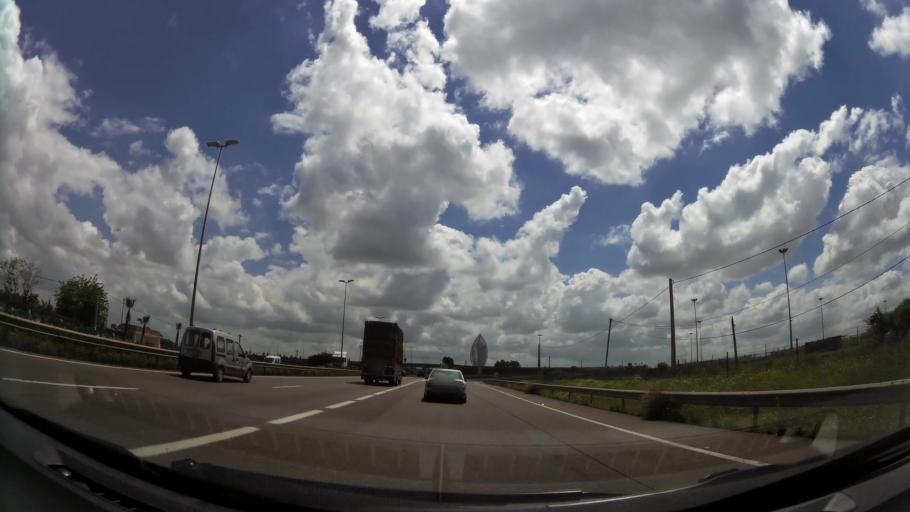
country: MA
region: Chaouia-Ouardigha
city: Nouaseur
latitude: 33.3929
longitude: -7.6203
